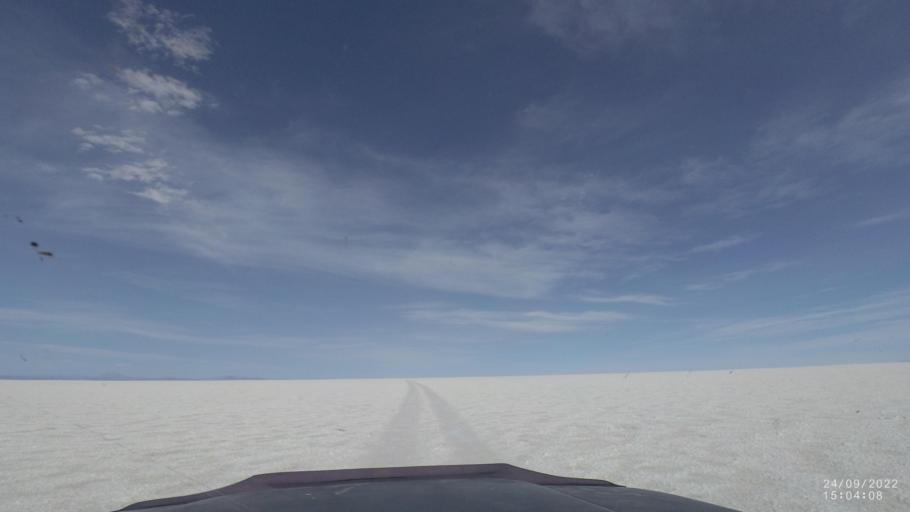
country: BO
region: Potosi
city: Colchani
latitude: -19.8984
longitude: -67.5259
